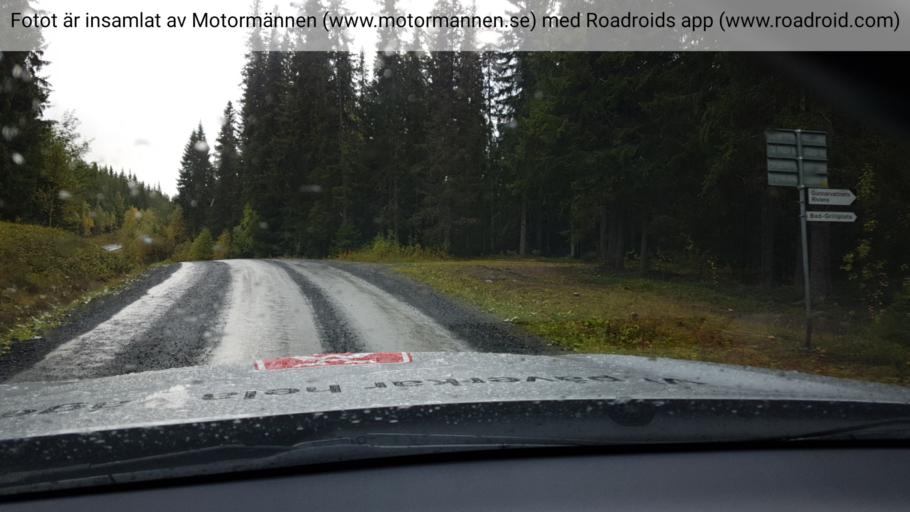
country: SE
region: Jaemtland
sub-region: Krokoms Kommun
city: Valla
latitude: 64.1084
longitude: 14.1506
